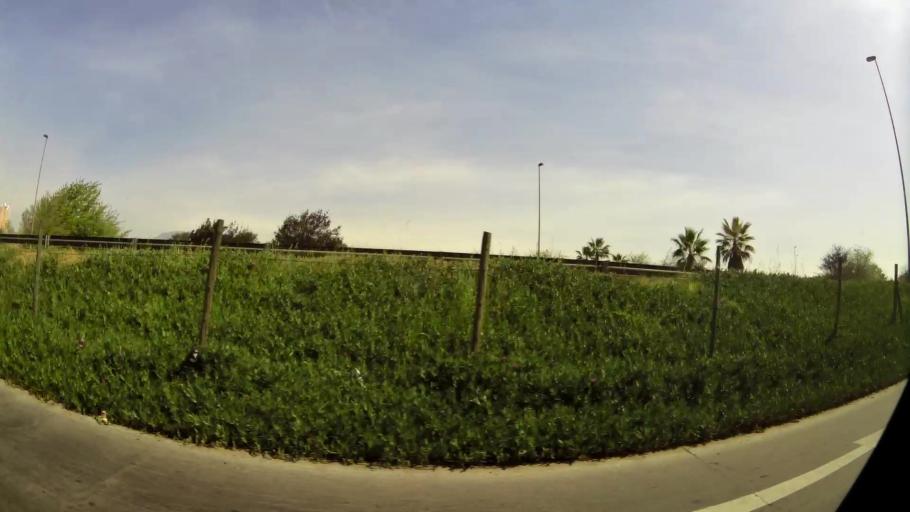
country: CL
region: Santiago Metropolitan
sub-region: Provincia de Santiago
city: Lo Prado
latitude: -33.4278
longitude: -70.7818
